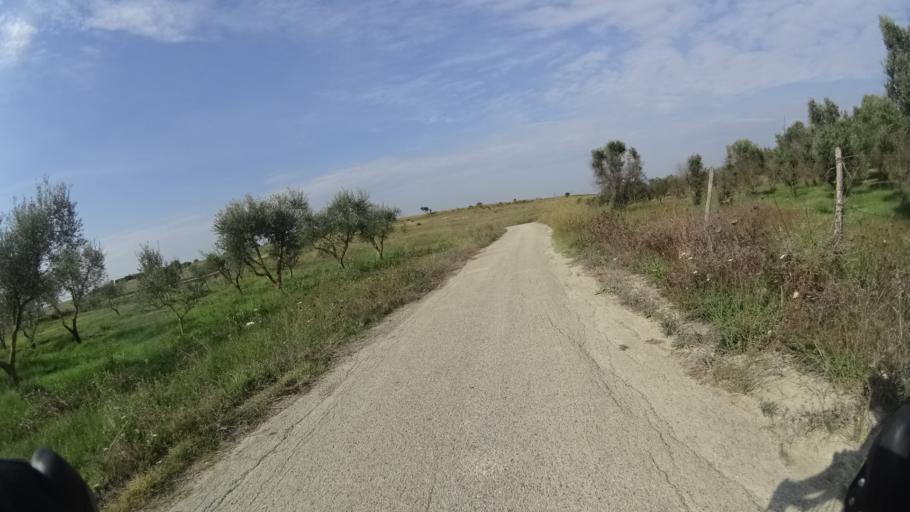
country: IT
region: Apulia
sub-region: Provincia di Taranto
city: Carosino
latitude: 40.4805
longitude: 17.4416
